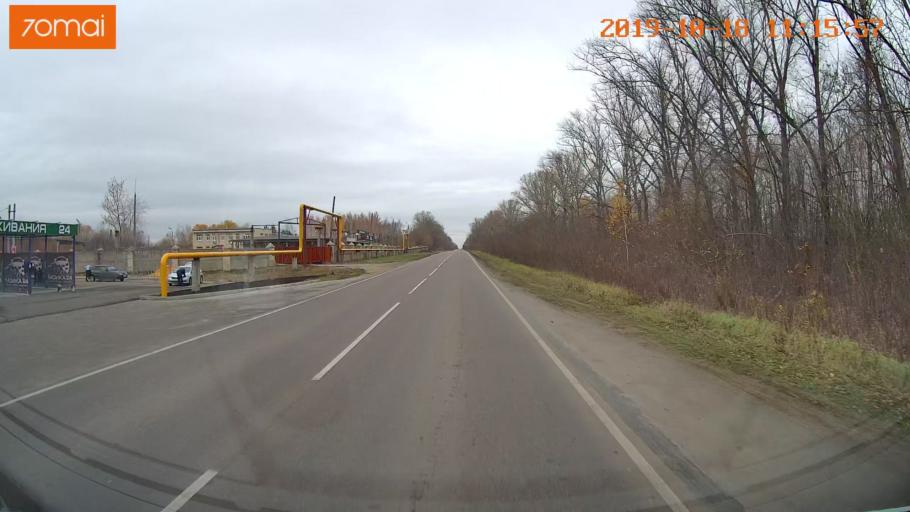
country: RU
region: Tula
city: Kimovsk
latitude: 54.0000
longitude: 38.5481
